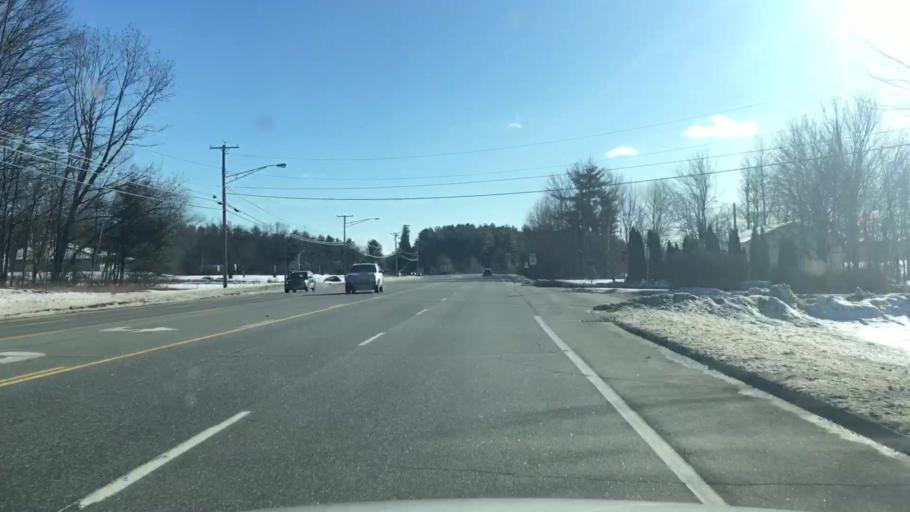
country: US
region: Maine
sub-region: Androscoggin County
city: Auburn
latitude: 44.1566
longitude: -70.2334
